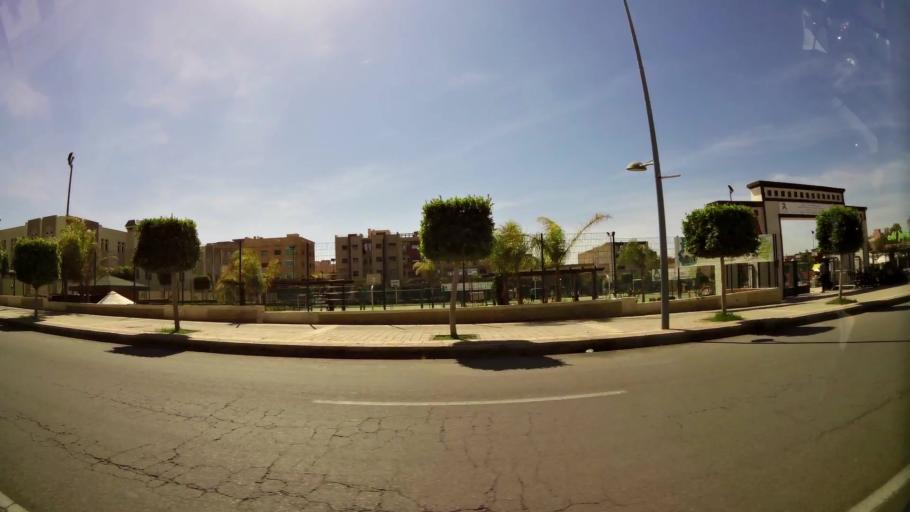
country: MA
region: Oriental
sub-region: Oujda-Angad
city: Oujda
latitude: 34.6590
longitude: -1.9123
